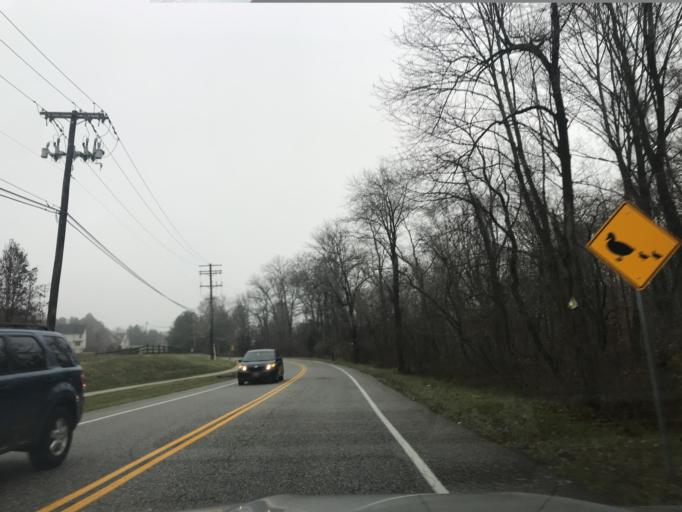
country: US
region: Maryland
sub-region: Harford County
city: South Bel Air
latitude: 39.5507
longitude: -76.3333
